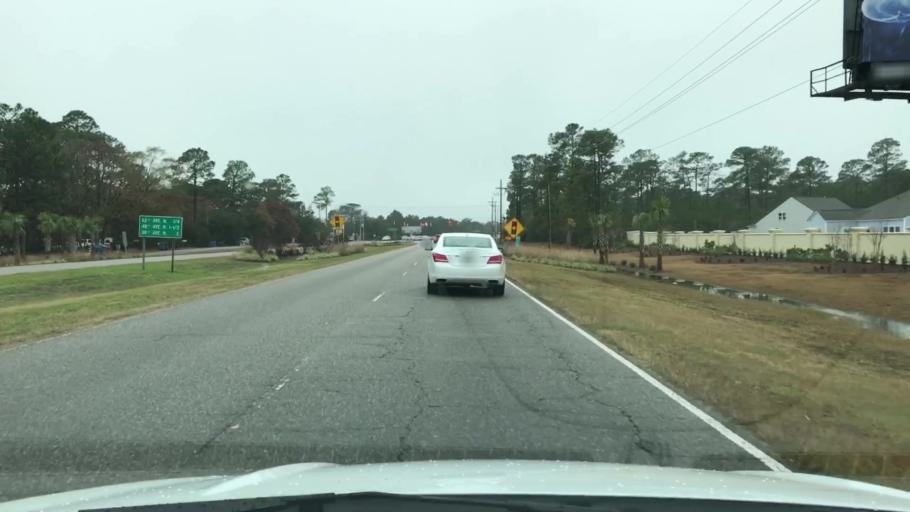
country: US
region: South Carolina
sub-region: Horry County
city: Myrtle Beach
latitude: 33.7456
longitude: -78.8382
